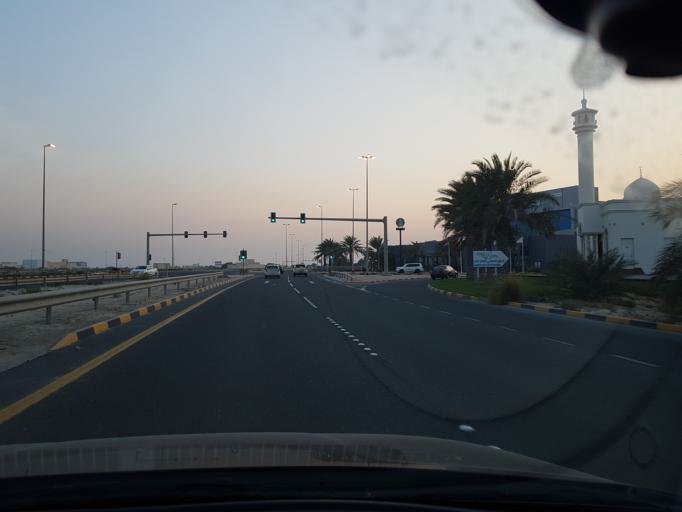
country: BH
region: Central Governorate
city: Dar Kulayb
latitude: 26.0281
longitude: 50.4971
